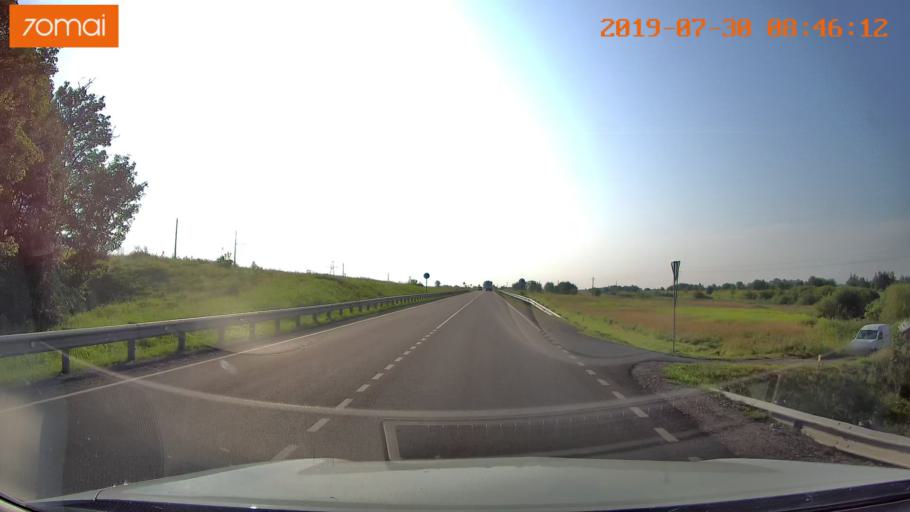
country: RU
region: Kaliningrad
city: Chernyakhovsk
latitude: 54.6246
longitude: 21.8798
